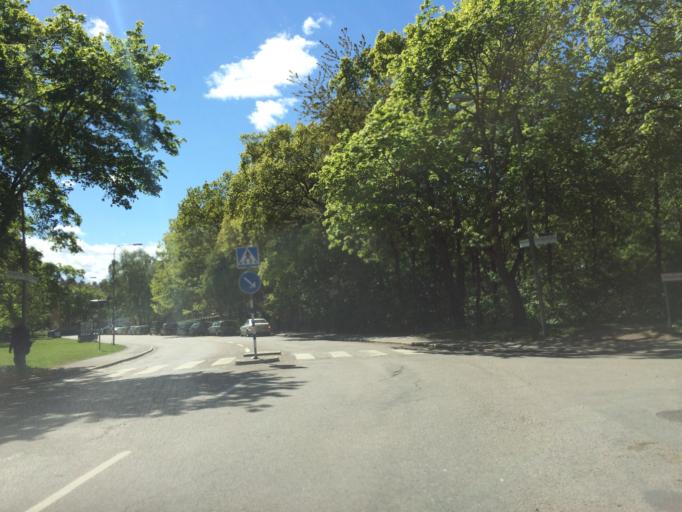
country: SE
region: Stockholm
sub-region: Solna Kommun
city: Solna
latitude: 59.3081
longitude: 17.9977
